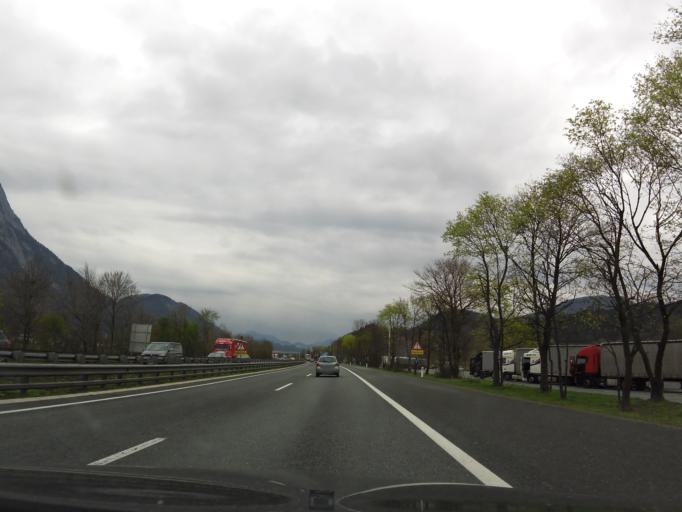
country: AT
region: Tyrol
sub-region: Politischer Bezirk Kufstein
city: Langkampfen
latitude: 47.5409
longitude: 12.1134
